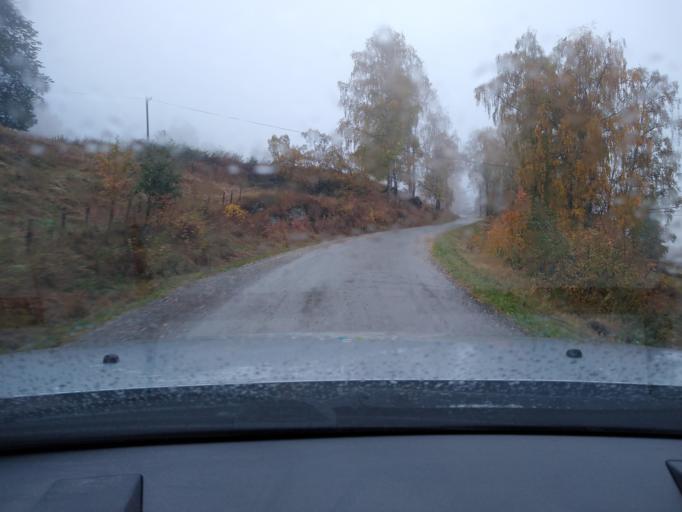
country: NO
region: Oppland
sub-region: Ringebu
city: Ringebu
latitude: 61.5311
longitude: 10.1496
